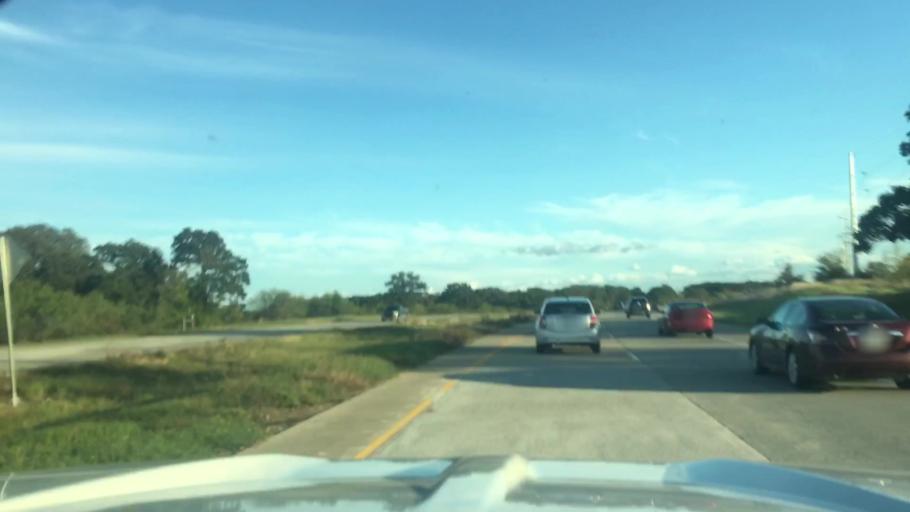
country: US
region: Texas
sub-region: Denton County
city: Denton
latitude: 33.2460
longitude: -97.0924
